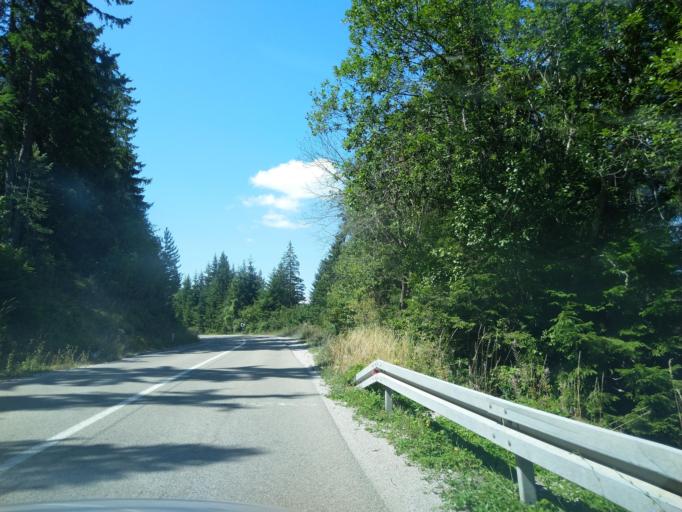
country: RS
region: Central Serbia
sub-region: Zlatiborski Okrug
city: Nova Varos
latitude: 43.3560
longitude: 19.8554
